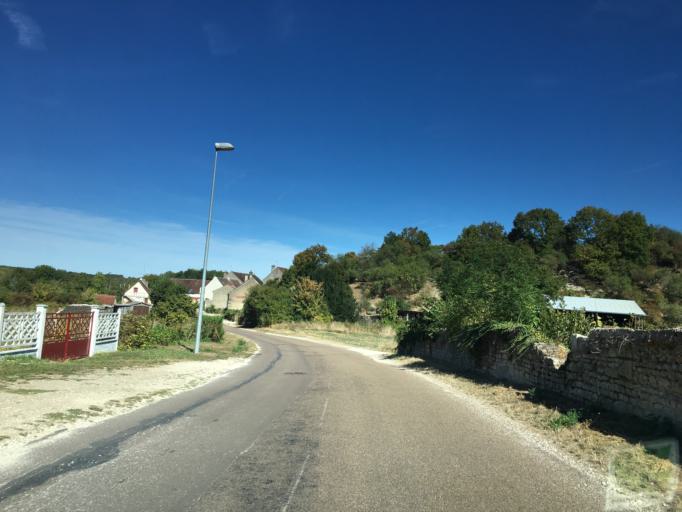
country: FR
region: Bourgogne
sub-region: Departement de l'Yonne
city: Vermenton
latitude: 47.5948
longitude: 3.6794
